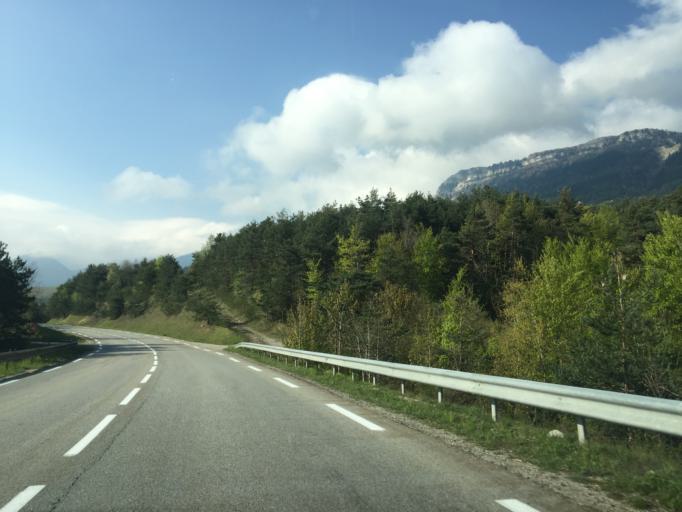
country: FR
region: Rhone-Alpes
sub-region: Departement de l'Isere
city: Mens
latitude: 44.8131
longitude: 5.6292
